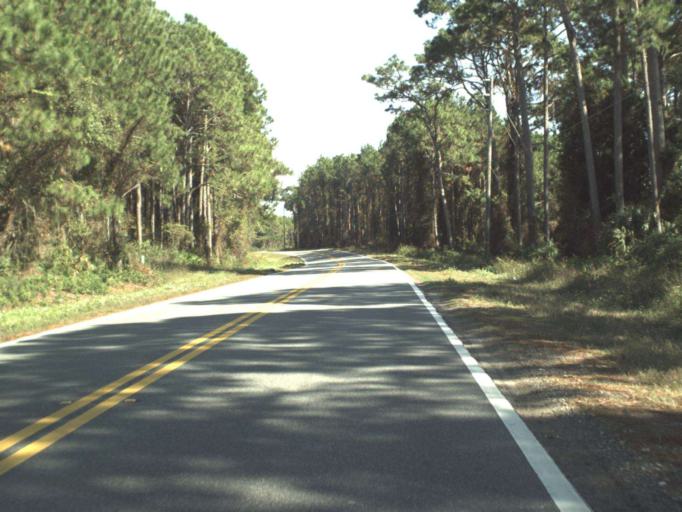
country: US
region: Florida
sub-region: Franklin County
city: Carrabelle
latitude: 29.9115
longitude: -84.5340
